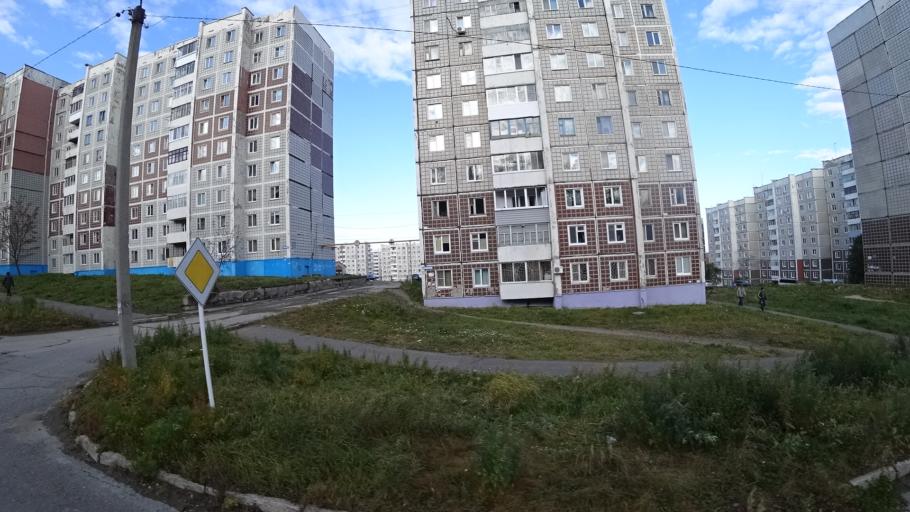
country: RU
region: Khabarovsk Krai
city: Amursk
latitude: 50.2475
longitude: 136.9224
